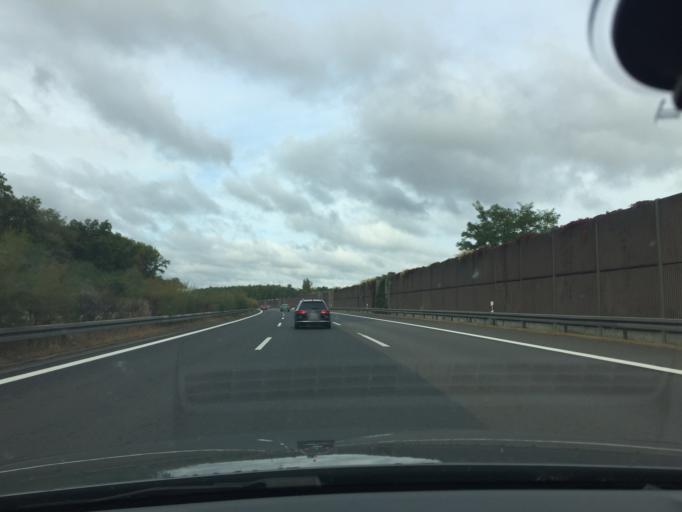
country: DE
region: Brandenburg
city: Woltersdorf
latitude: 52.4600
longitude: 13.7956
